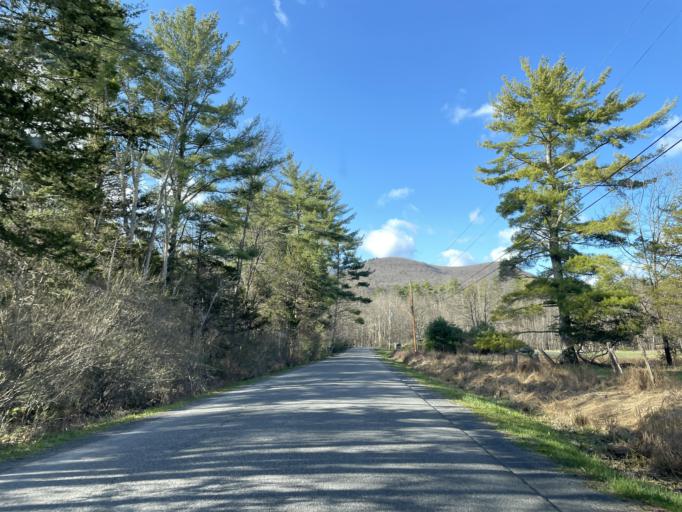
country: US
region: New York
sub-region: Ulster County
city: Woodstock
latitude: 42.0439
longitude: -74.1408
